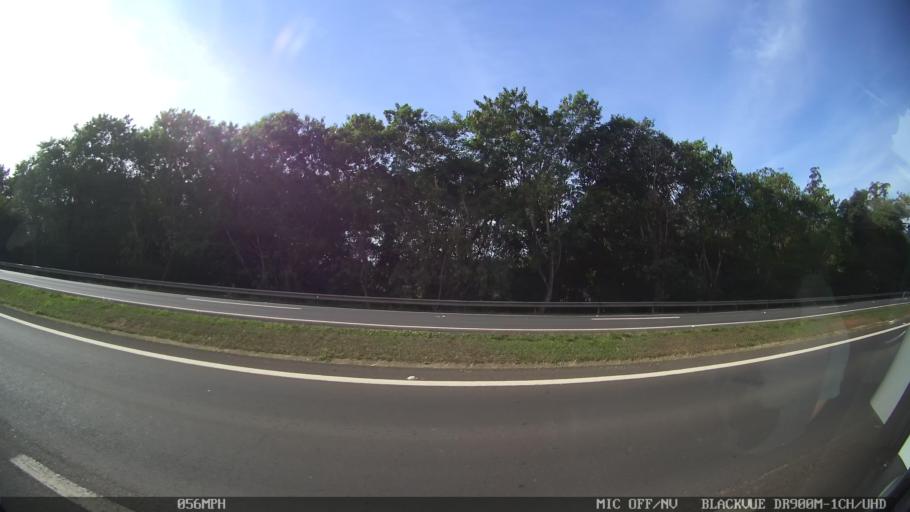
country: BR
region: Sao Paulo
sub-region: Piracicaba
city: Piracicaba
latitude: -22.7718
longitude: -47.6484
